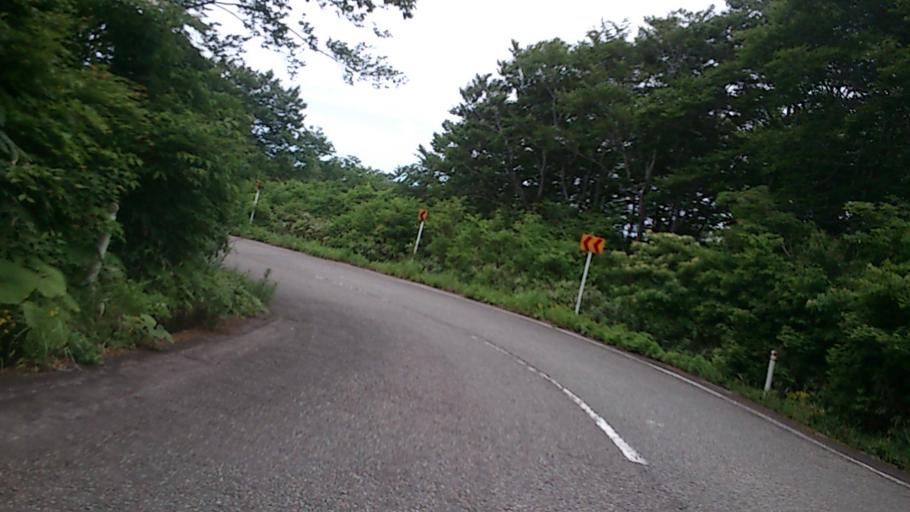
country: JP
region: Yamagata
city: Yuza
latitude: 39.1103
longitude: 139.9659
